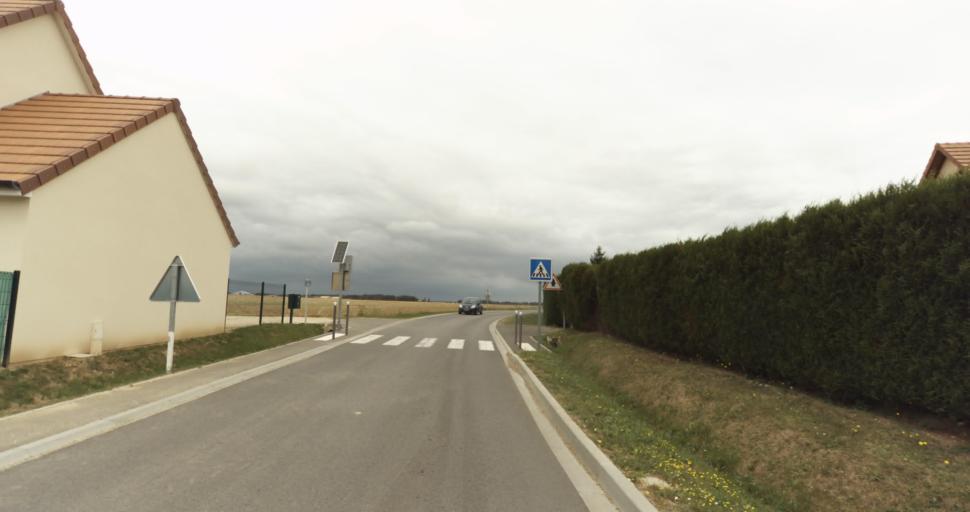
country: FR
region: Haute-Normandie
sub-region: Departement de l'Eure
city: Gravigny
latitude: 49.0332
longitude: 1.2400
